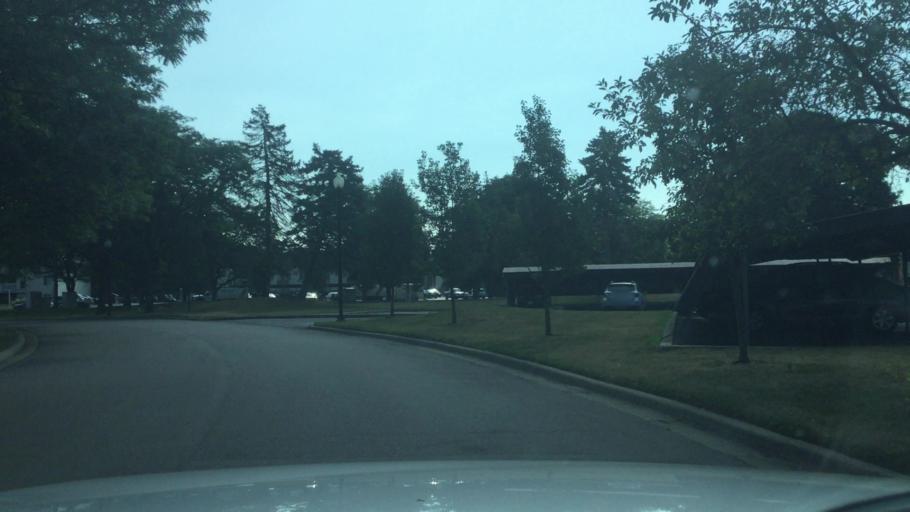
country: US
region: Michigan
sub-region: Washtenaw County
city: Ypsilanti
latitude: 42.2136
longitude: -83.5672
